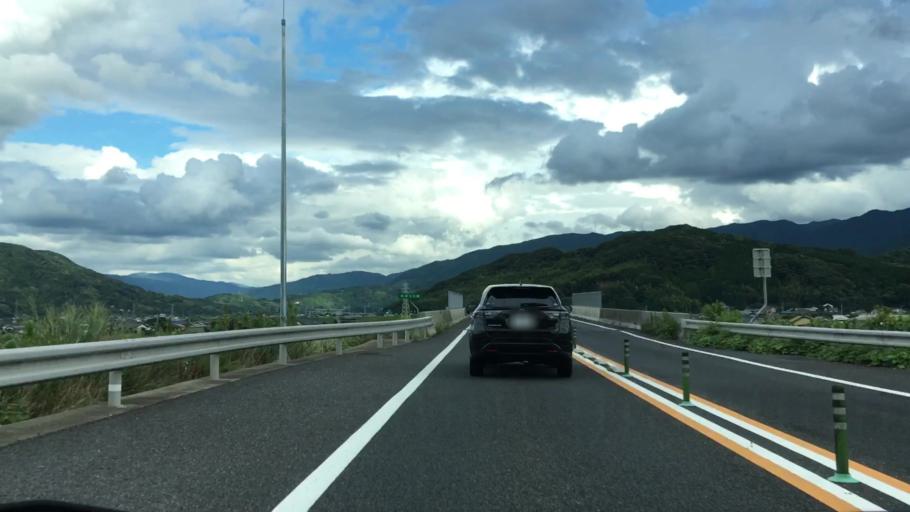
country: JP
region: Saga Prefecture
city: Karatsu
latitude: 33.4120
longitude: 129.9841
